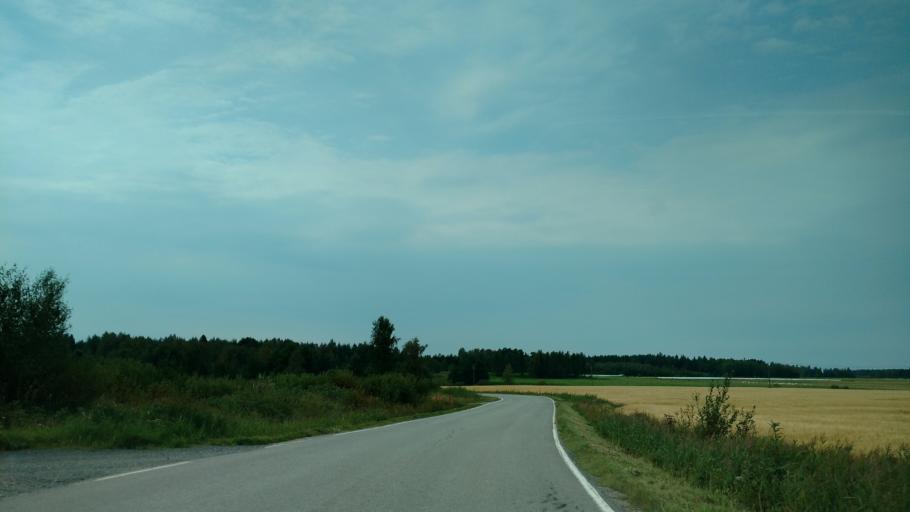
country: FI
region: Varsinais-Suomi
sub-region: Loimaa
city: Koski Tl
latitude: 60.6888
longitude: 23.1617
